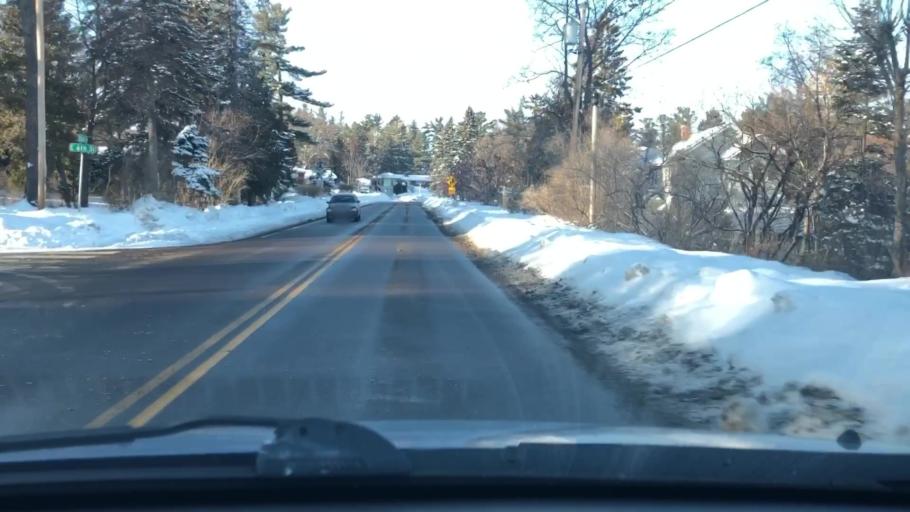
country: US
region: Minnesota
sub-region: Saint Louis County
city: Duluth
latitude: 46.8176
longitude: -92.0696
